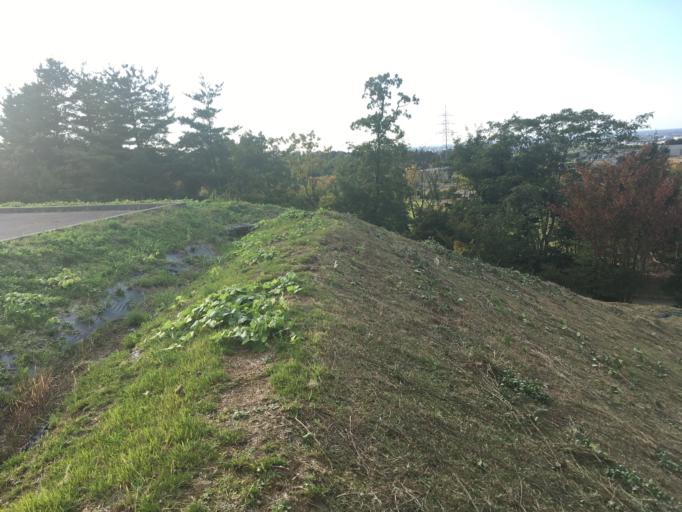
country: JP
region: Ishikawa
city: Tsurugi-asahimachi
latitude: 36.4470
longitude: 136.5909
